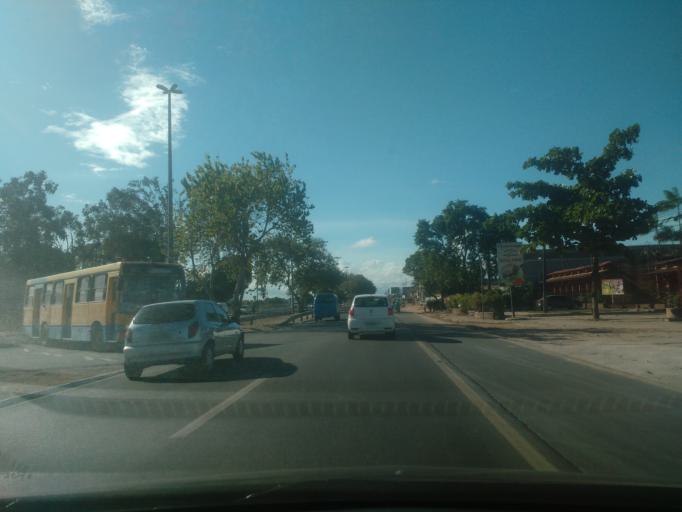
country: BR
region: Alagoas
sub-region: Satuba
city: Satuba
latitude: -9.5372
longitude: -35.7930
